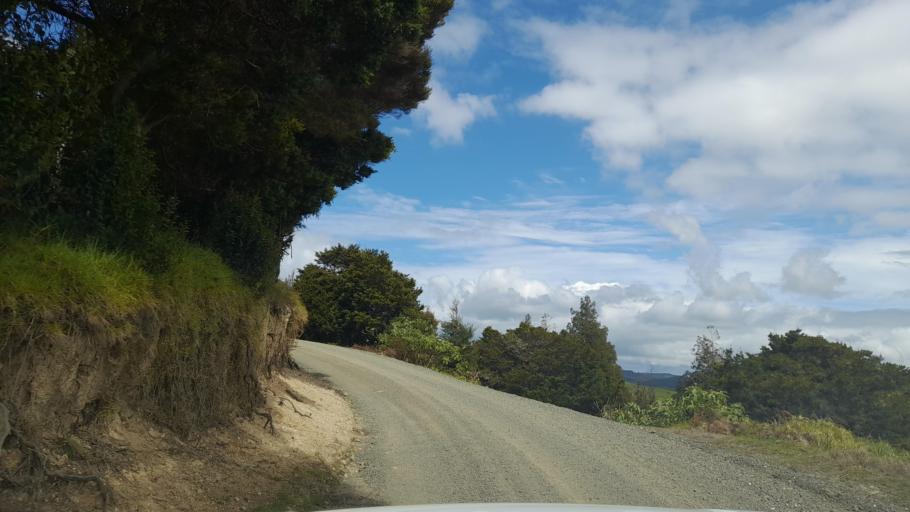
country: NZ
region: Auckland
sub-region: Auckland
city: Wellsford
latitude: -36.2079
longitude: 174.3348
